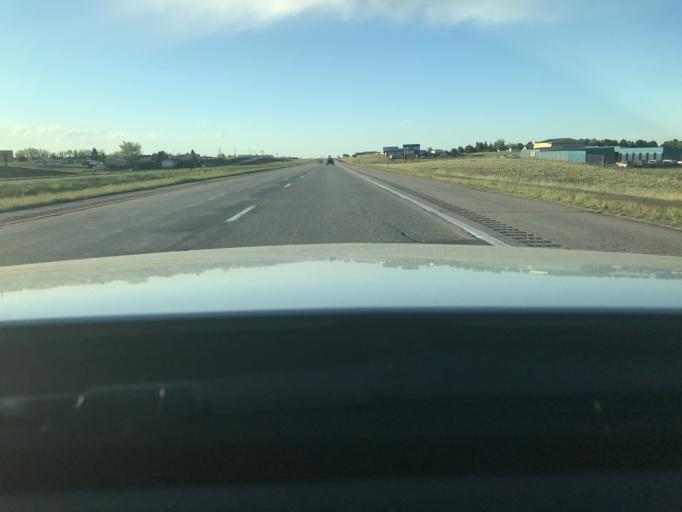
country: US
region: Wyoming
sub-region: Platte County
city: Wheatland
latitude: 42.0310
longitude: -104.9652
